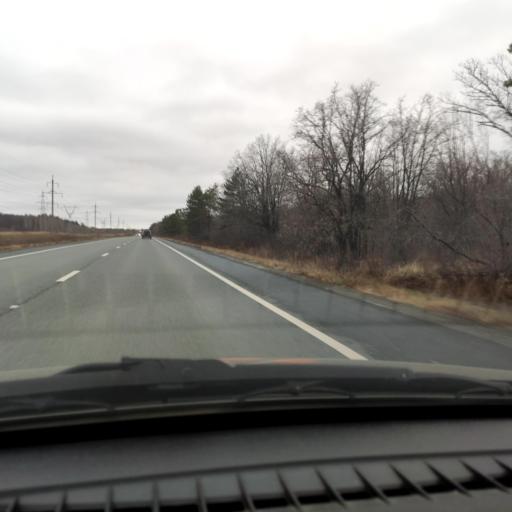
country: RU
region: Samara
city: Bogatyr'
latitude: 53.5026
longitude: 49.9473
